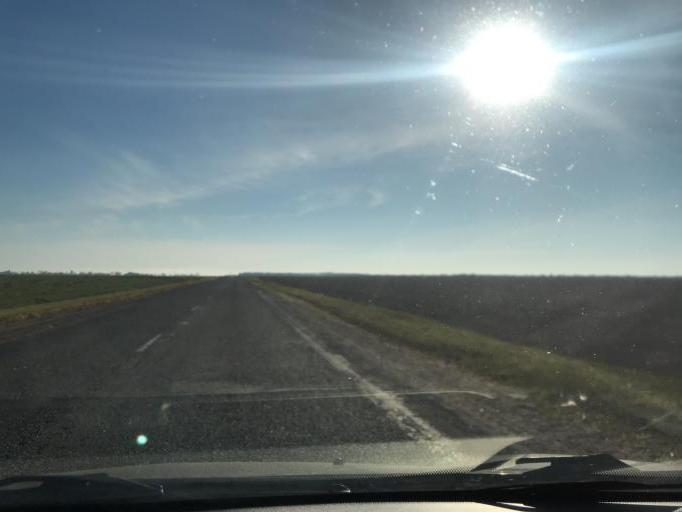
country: BY
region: Gomel
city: Brahin
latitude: 51.7911
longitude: 30.1755
